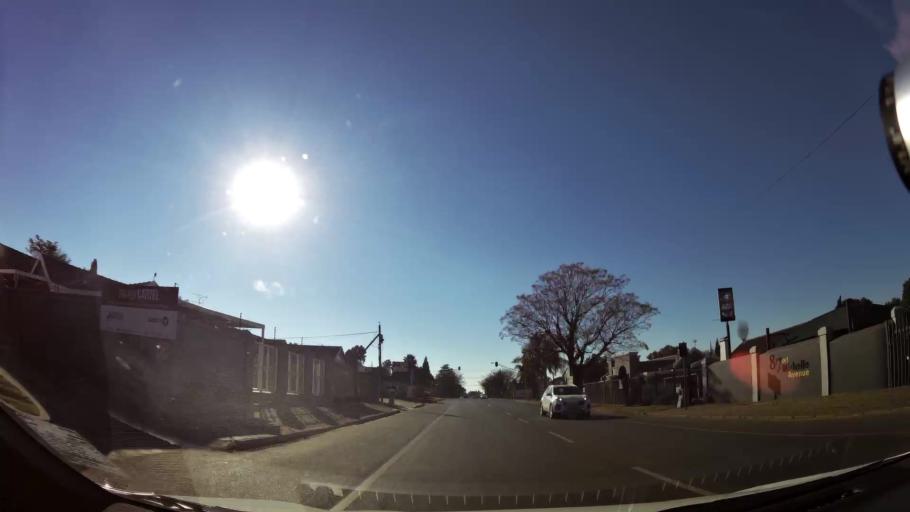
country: ZA
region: Gauteng
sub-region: Ekurhuleni Metropolitan Municipality
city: Germiston
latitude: -26.2860
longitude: 28.1077
